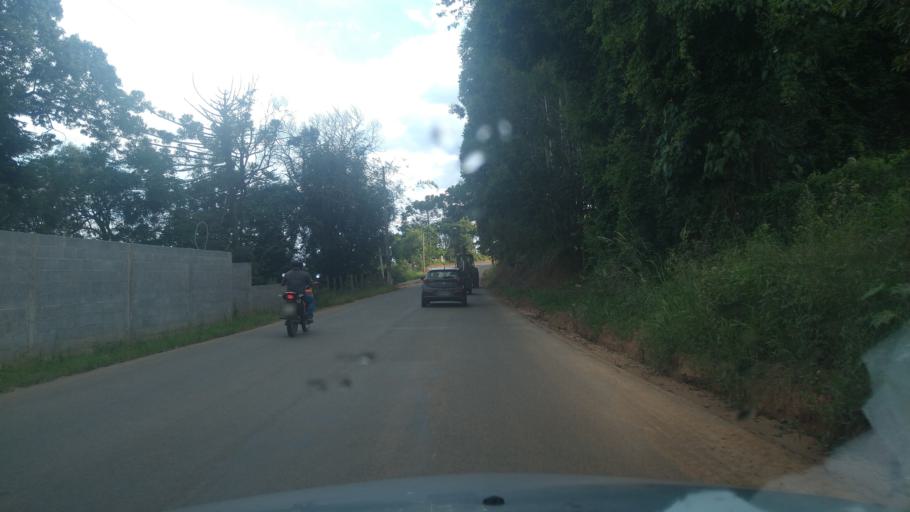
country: BR
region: Minas Gerais
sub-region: Extrema
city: Extrema
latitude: -22.7368
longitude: -46.3695
